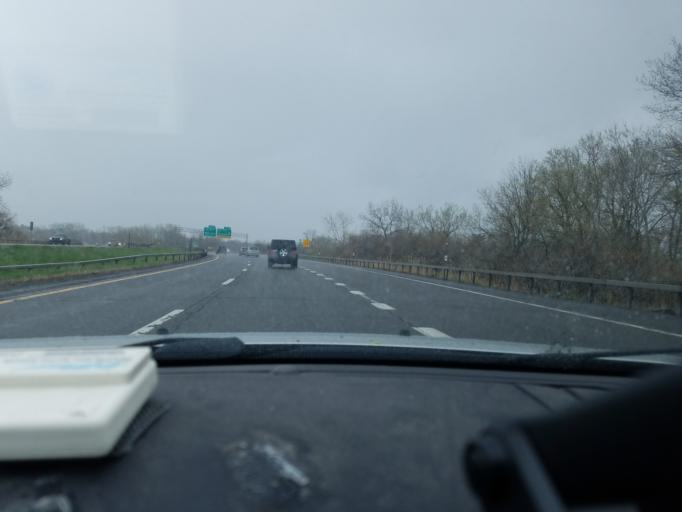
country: US
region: New York
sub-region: Onondaga County
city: North Syracuse
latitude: 43.1434
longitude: -76.1196
